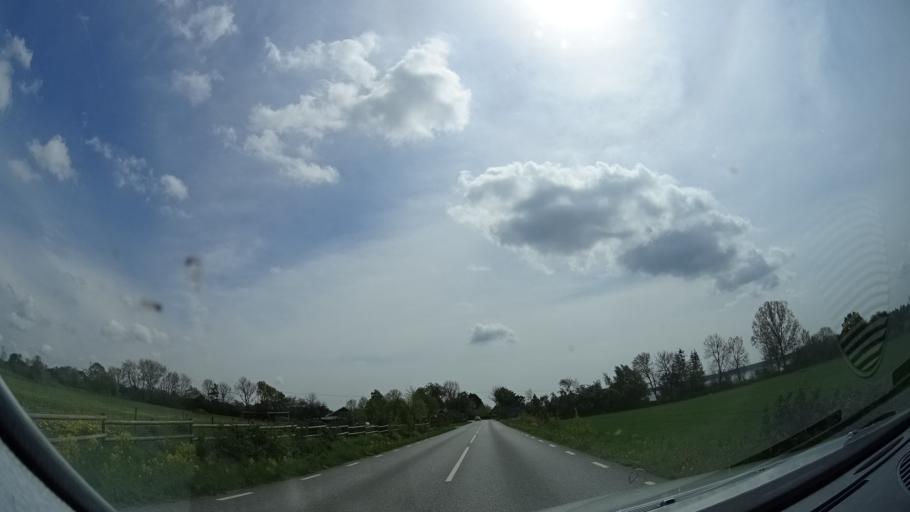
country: SE
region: Skane
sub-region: Hoors Kommun
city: Loberod
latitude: 55.7074
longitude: 13.5576
